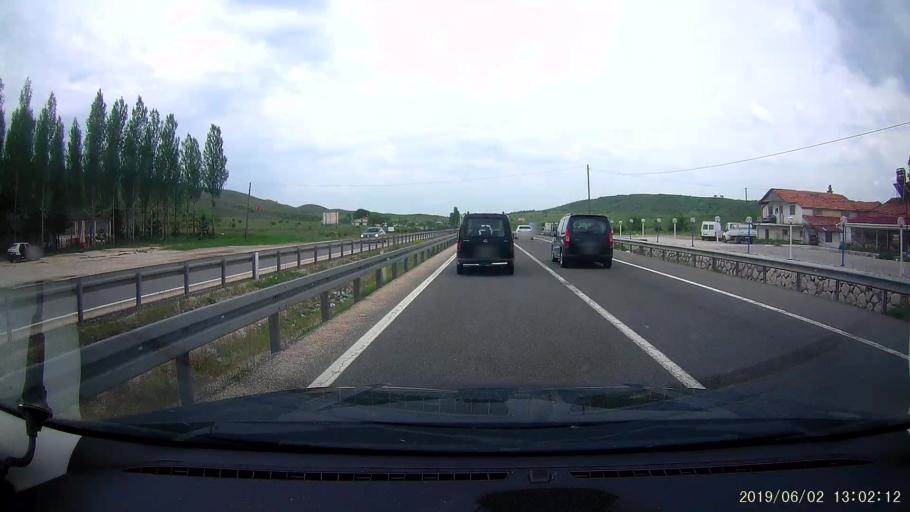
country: TR
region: Karabuk
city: Gozyeri
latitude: 40.8533
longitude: 32.4781
